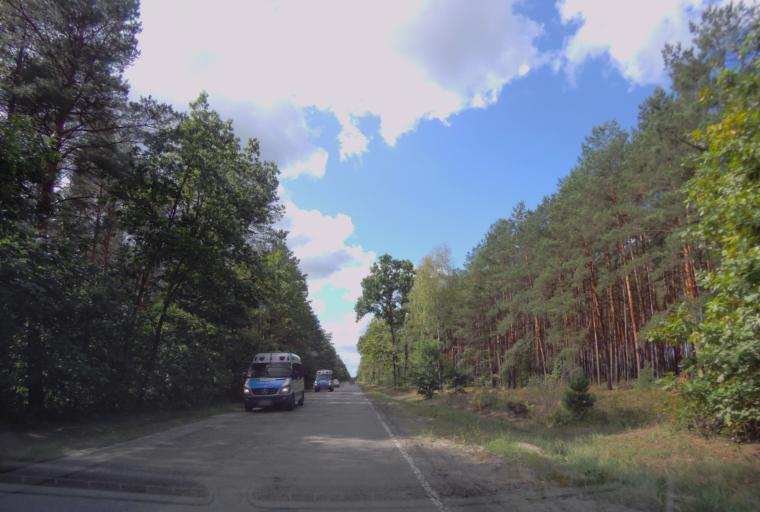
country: PL
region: Subcarpathian Voivodeship
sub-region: Powiat stalowowolski
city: Bojanow
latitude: 50.4226
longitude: 21.8987
